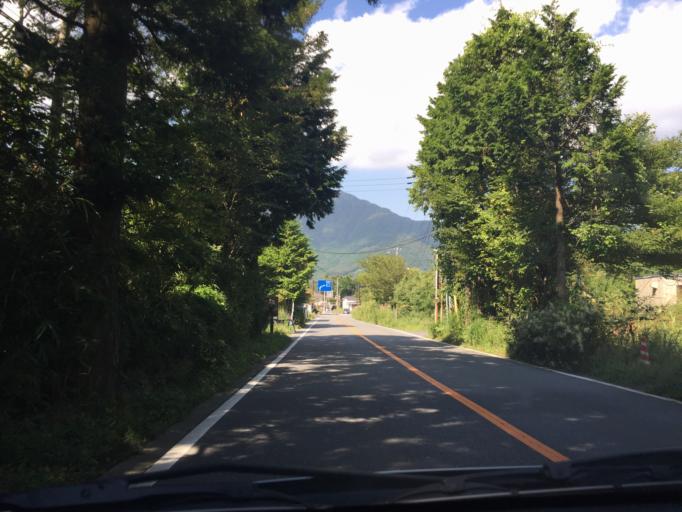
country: JP
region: Shizuoka
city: Gotemba
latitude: 35.2573
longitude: 139.0007
